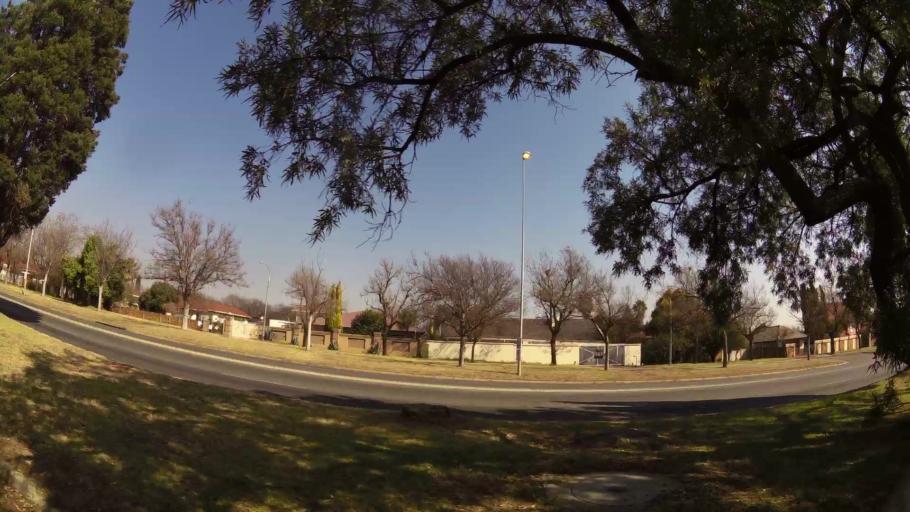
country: ZA
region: Gauteng
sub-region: Ekurhuleni Metropolitan Municipality
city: Boksburg
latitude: -26.2412
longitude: 28.2619
